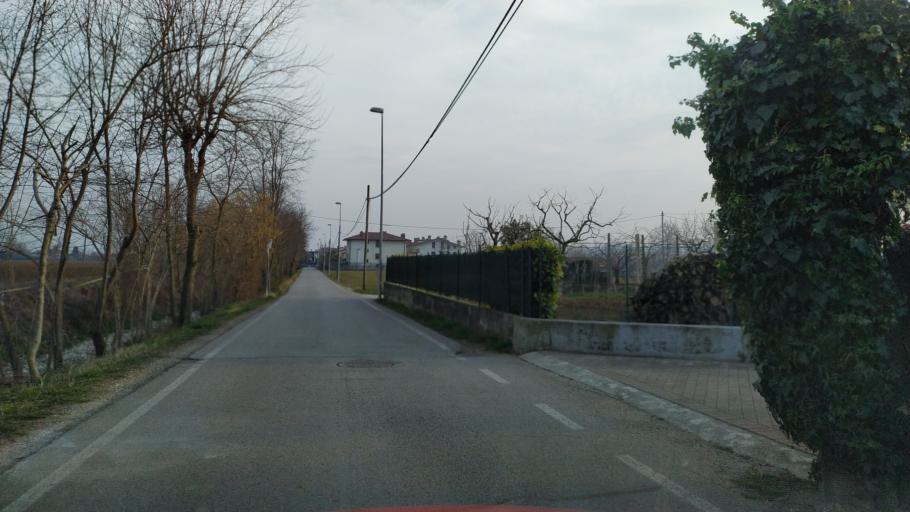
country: IT
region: Veneto
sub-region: Provincia di Vicenza
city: Marano Vicentino
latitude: 45.6838
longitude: 11.4329
